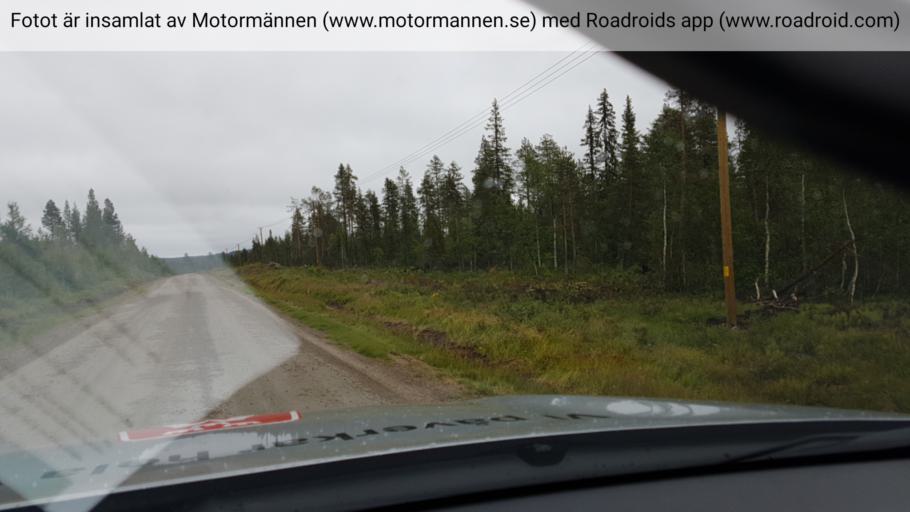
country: SE
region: Norrbotten
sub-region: Gallivare Kommun
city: Gaellivare
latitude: 66.7076
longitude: 20.4559
